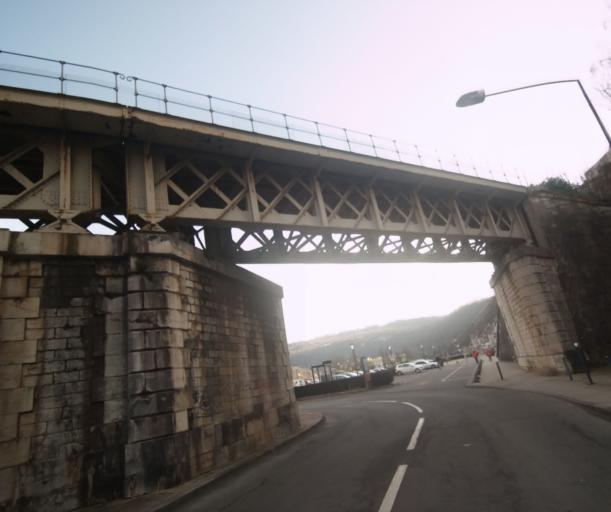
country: FR
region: Franche-Comte
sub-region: Departement du Doubs
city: Besancon
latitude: 47.2340
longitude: 6.0336
